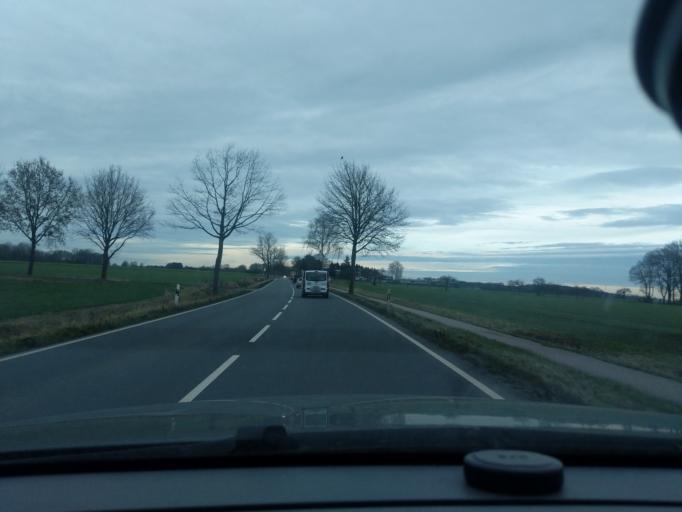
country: DE
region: Lower Saxony
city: Sauensiek
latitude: 53.3700
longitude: 9.5932
